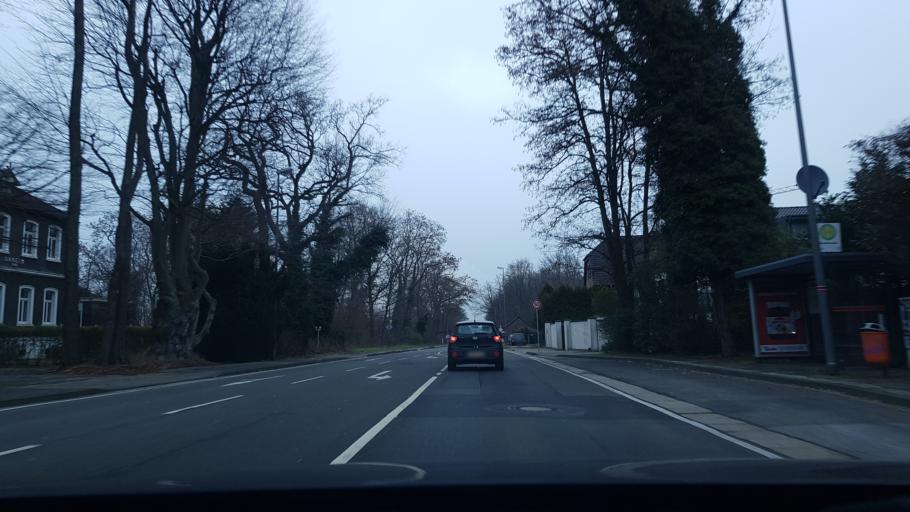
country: DE
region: North Rhine-Westphalia
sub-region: Regierungsbezirk Dusseldorf
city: Moers
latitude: 51.4318
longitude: 6.6478
